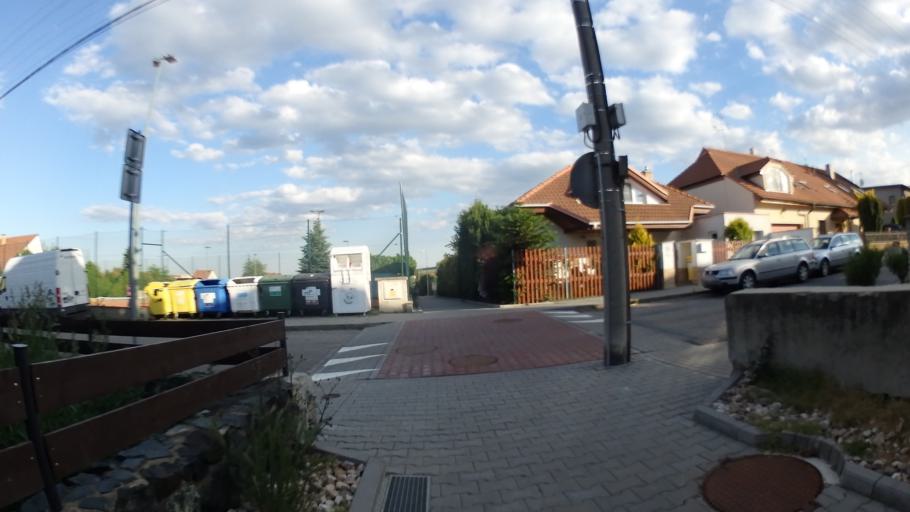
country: CZ
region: South Moravian
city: Moravany
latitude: 49.1484
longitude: 16.5779
